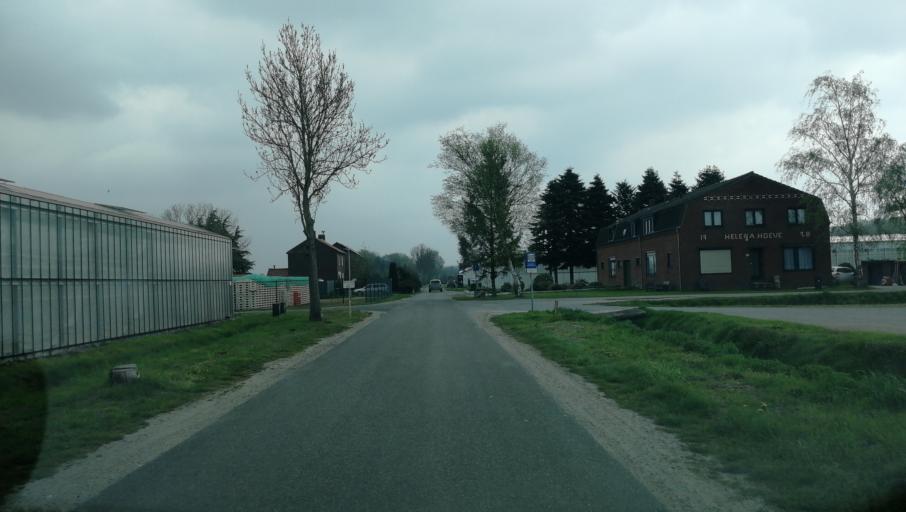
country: NL
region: Limburg
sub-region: Gemeente Venlo
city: Venlo
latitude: 51.3966
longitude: 6.2192
